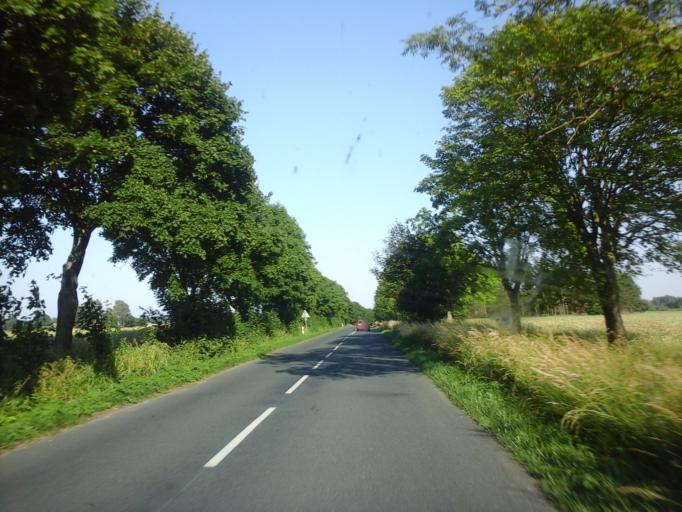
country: PL
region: West Pomeranian Voivodeship
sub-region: Powiat stargardzki
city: Dobrzany
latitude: 53.4247
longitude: 15.4173
